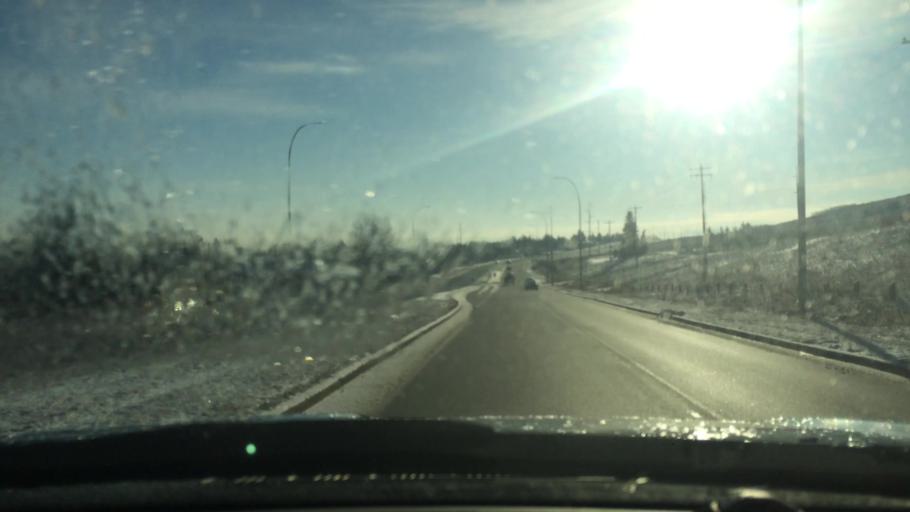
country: CA
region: Alberta
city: Calgary
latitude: 51.1266
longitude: -114.1009
